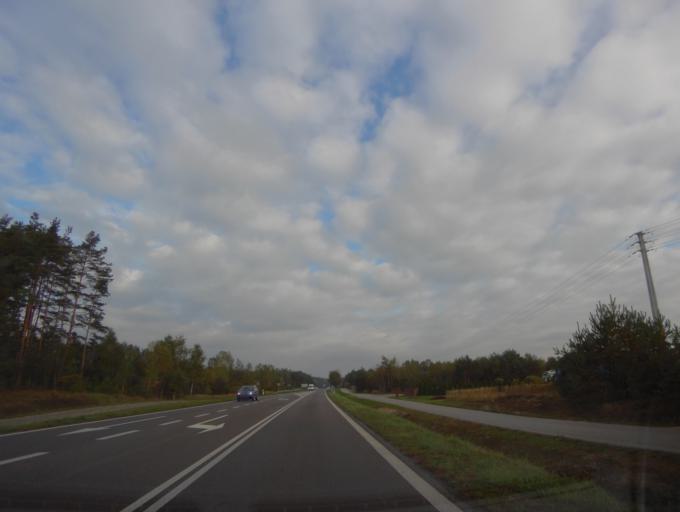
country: PL
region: Lublin Voivodeship
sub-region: Powiat bilgorajski
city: Bilgoraj
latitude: 50.5783
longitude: 22.6861
